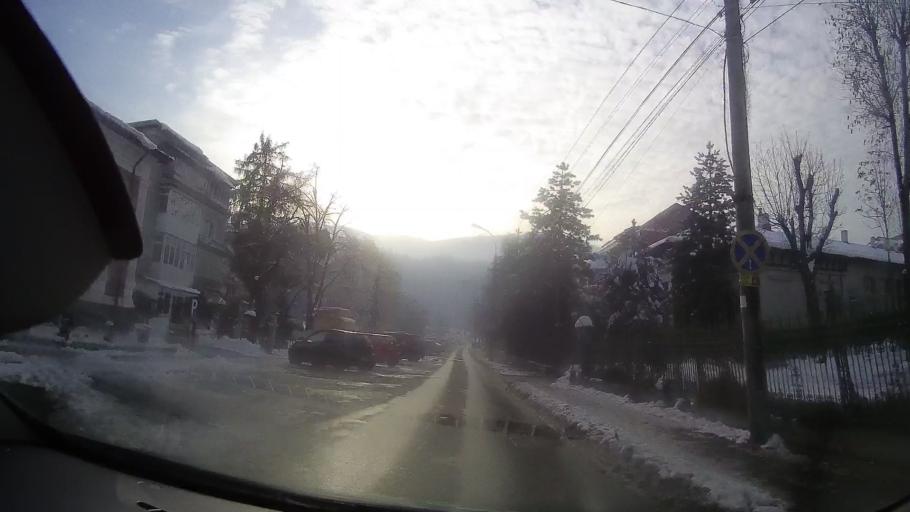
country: RO
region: Neamt
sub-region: Municipiul Piatra-Neamt
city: Valeni
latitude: 46.9259
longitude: 26.3669
